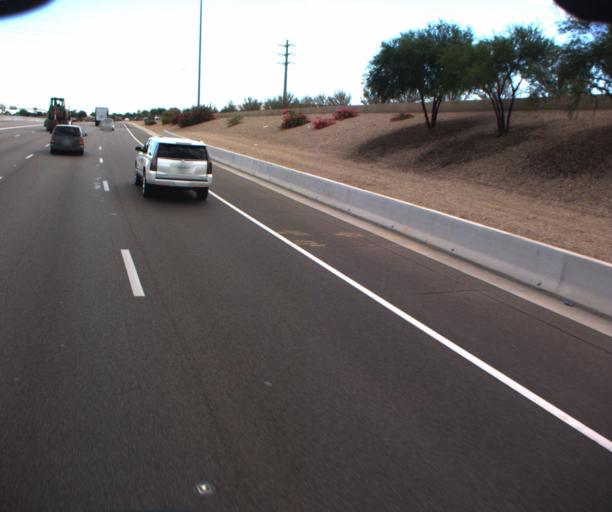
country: US
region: Arizona
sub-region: Maricopa County
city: Chandler
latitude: 33.2902
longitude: -111.8860
